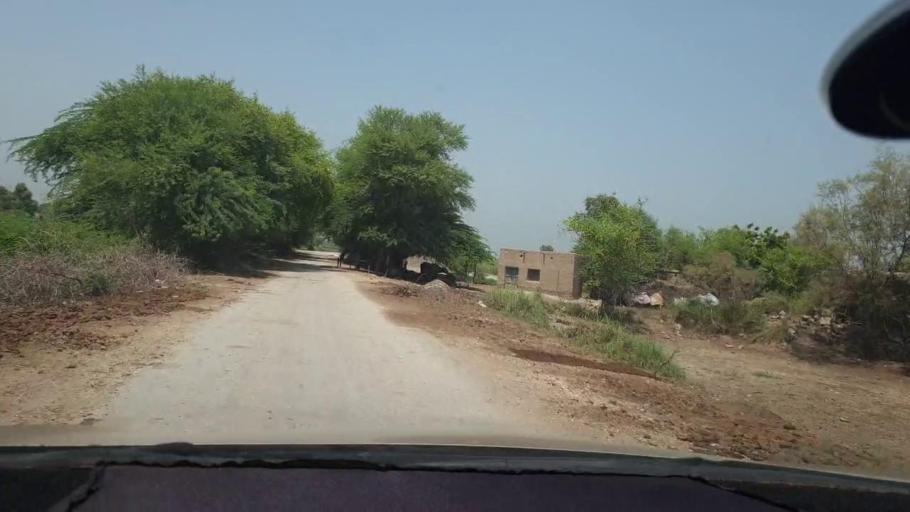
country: PK
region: Sindh
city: Kambar
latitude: 27.6671
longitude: 67.9143
